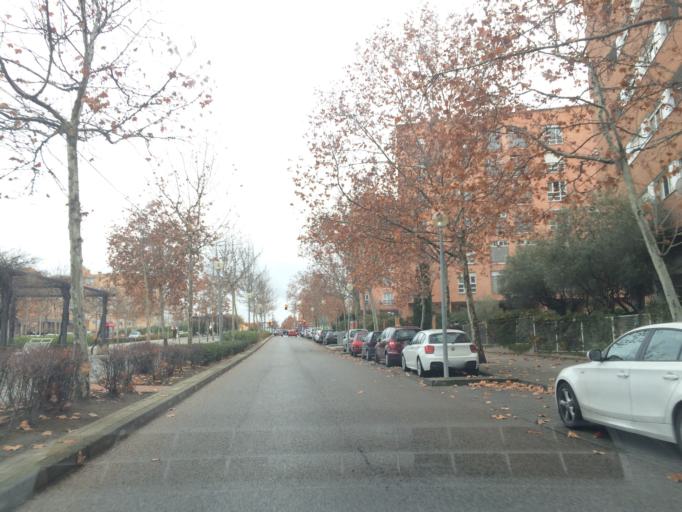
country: ES
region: Madrid
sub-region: Provincia de Madrid
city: Tres Cantos
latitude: 40.6013
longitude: -3.7134
